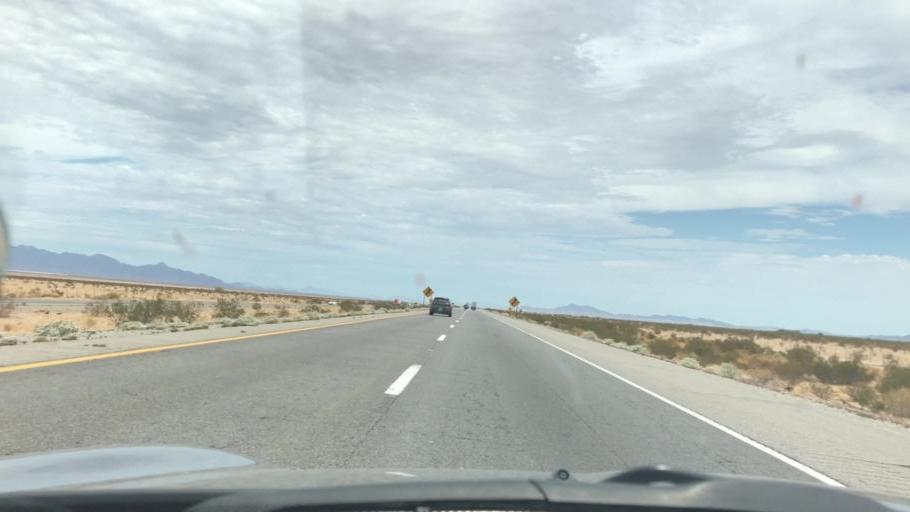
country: US
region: California
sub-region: Riverside County
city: Mesa Verde
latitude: 33.6386
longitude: -115.0927
